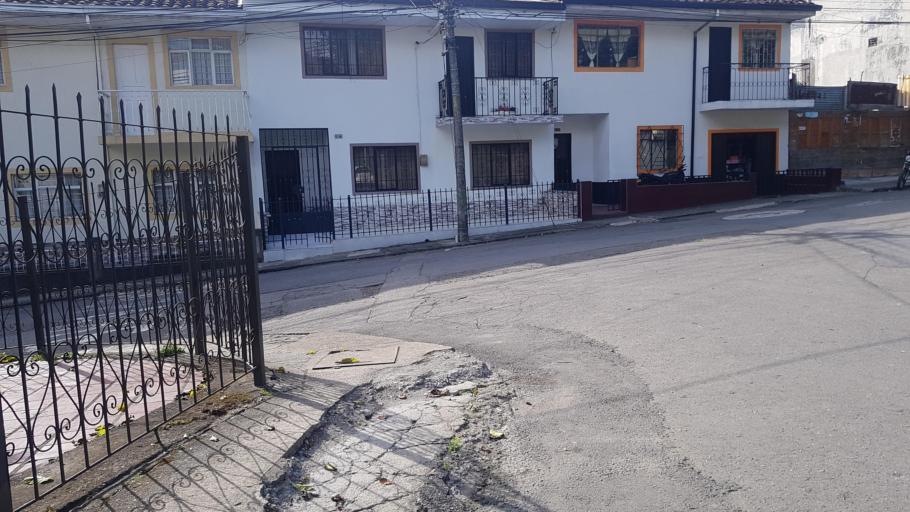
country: CO
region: Cauca
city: Popayan
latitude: 2.4401
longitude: -76.6127
